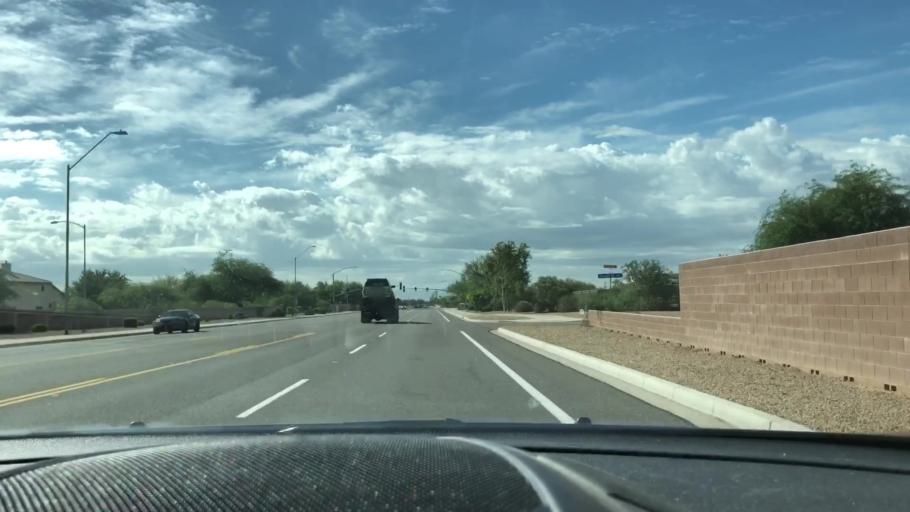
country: US
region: Arizona
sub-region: Maricopa County
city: Sun City
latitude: 33.6984
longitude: -112.2378
